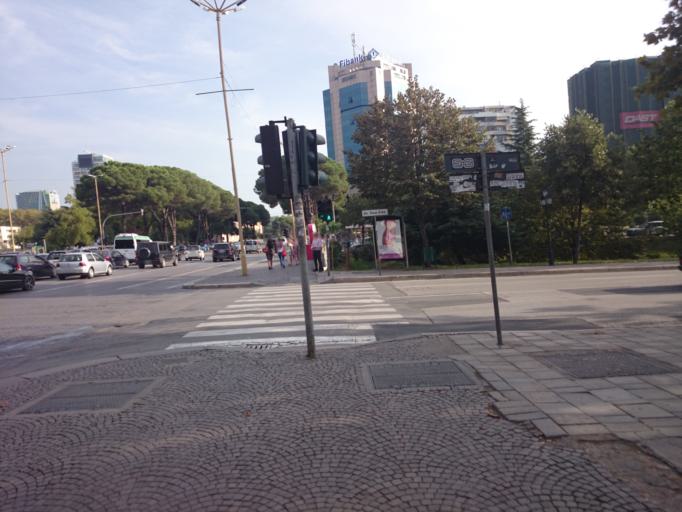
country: AL
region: Tirane
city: Tirana
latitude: 41.3242
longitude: 19.8193
